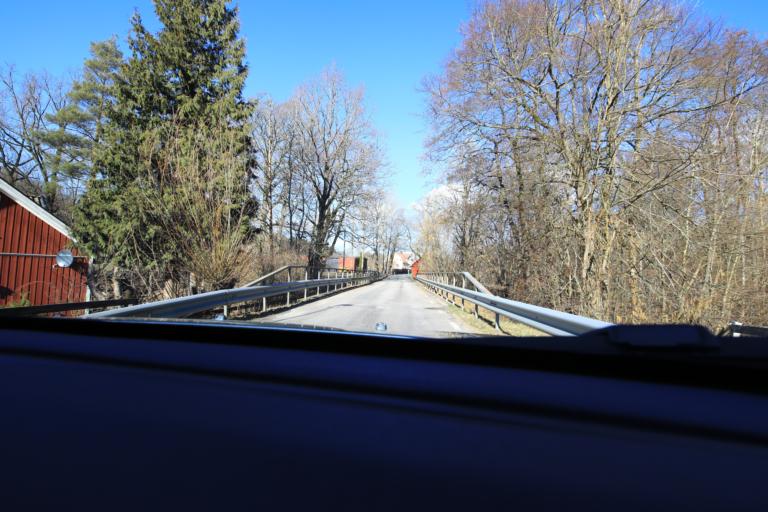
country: SE
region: Halland
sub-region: Varbergs Kommun
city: Tvaaker
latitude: 57.0650
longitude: 12.4859
